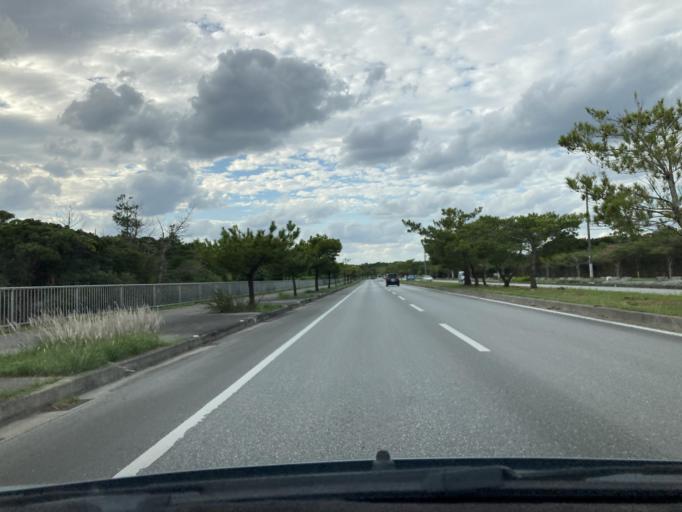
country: JP
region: Okinawa
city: Okinawa
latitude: 26.3645
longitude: 127.7899
